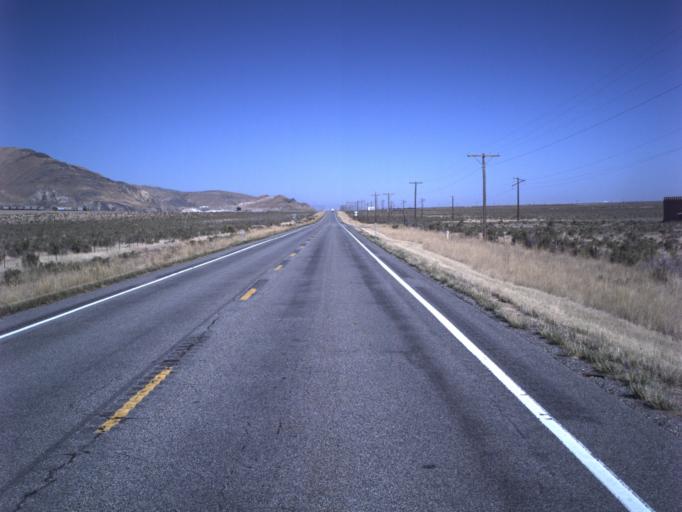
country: US
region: Utah
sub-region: Tooele County
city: Grantsville
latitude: 40.6628
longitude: -112.5409
